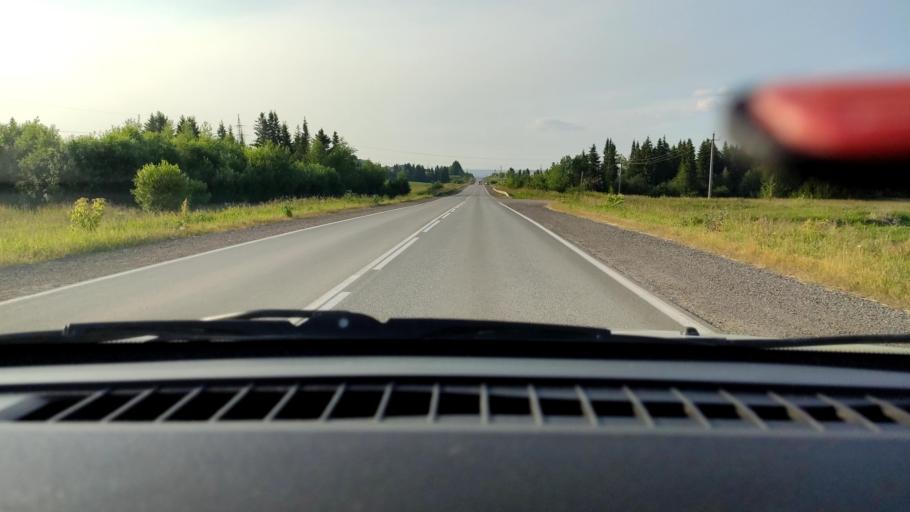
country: RU
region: Perm
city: Lobanovo
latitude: 57.8515
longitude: 56.2963
